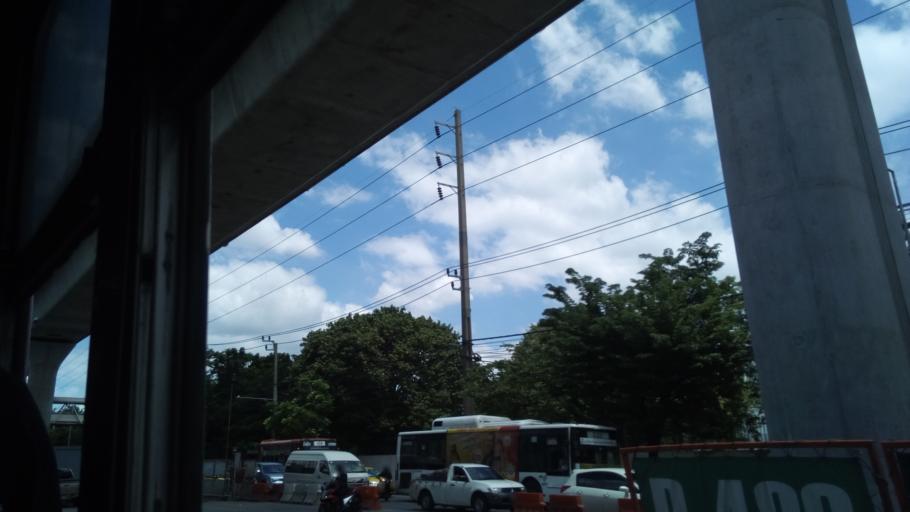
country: TH
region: Bangkok
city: Sai Mai
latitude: 13.9167
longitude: 100.6210
